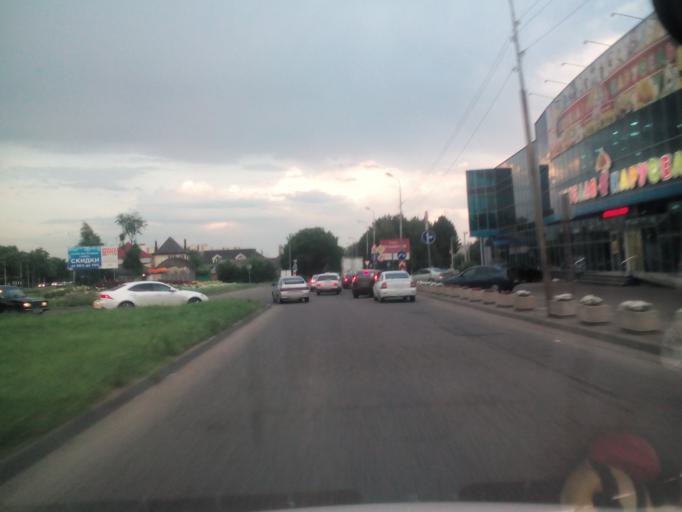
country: RU
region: Stavropol'skiy
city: Svobody
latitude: 44.0405
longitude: 43.0338
